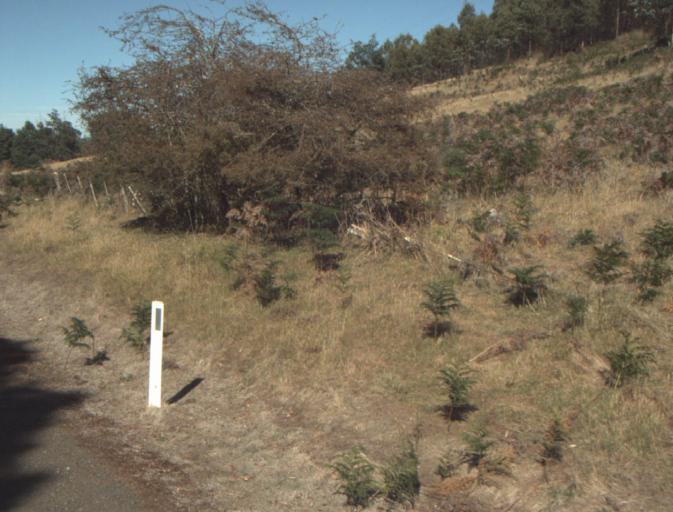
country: AU
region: Tasmania
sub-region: Dorset
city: Scottsdale
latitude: -41.2892
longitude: 147.3599
